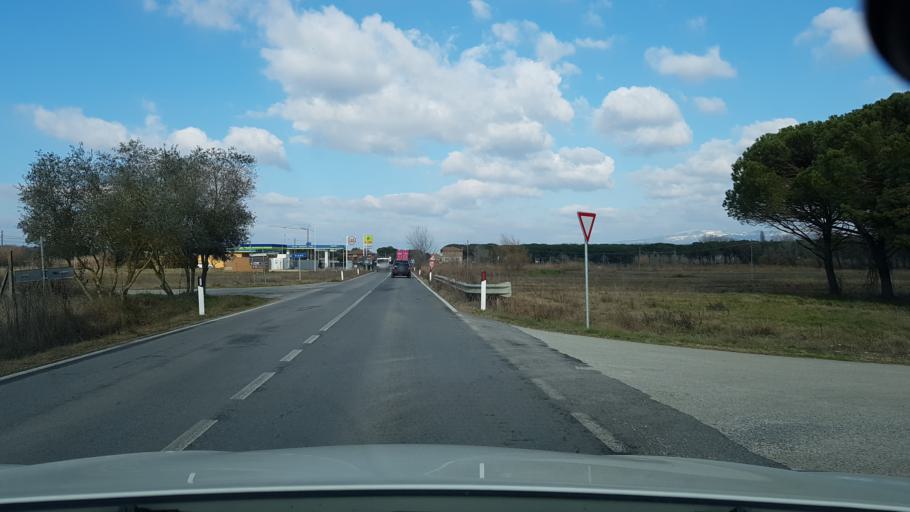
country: IT
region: Umbria
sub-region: Provincia di Perugia
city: Castiglione del Lago
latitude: 43.1482
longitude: 12.0229
